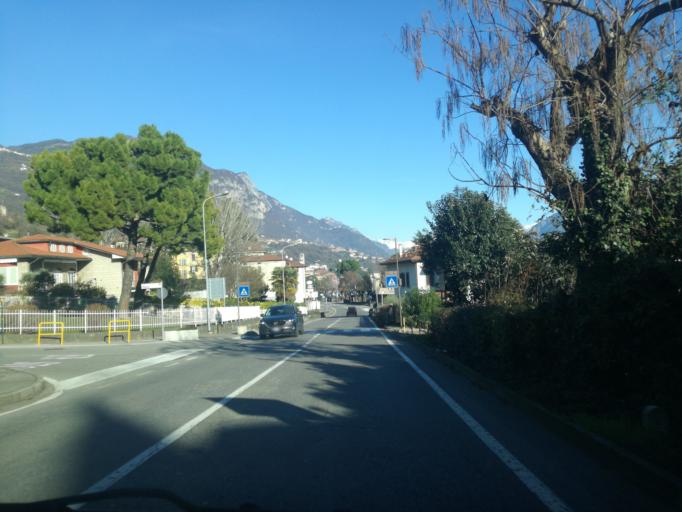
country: IT
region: Lombardy
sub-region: Provincia di Bergamo
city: Lovere
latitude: 45.8111
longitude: 10.0701
